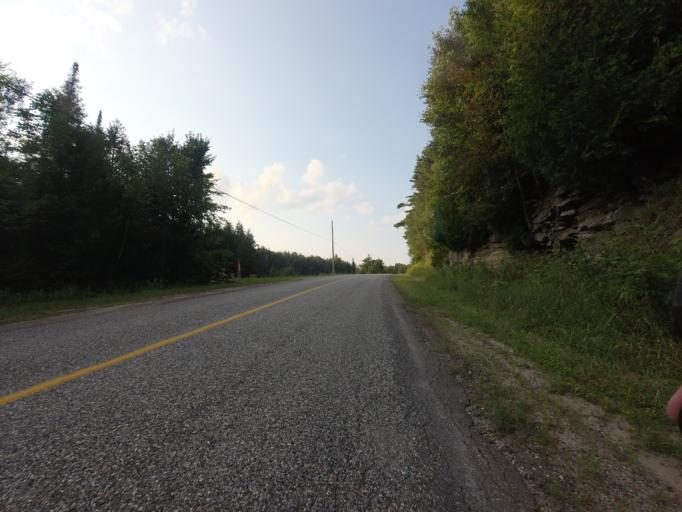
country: CA
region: Ontario
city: Renfrew
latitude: 44.9841
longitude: -76.7404
